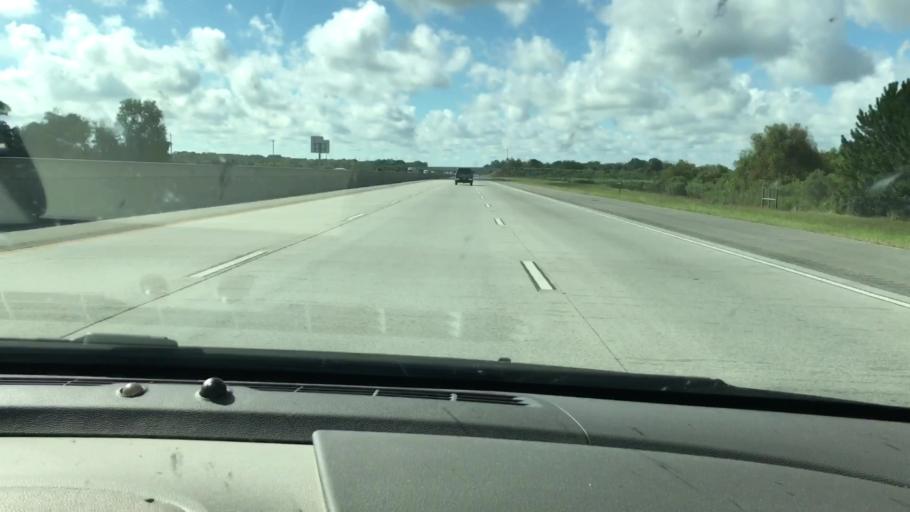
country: US
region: Georgia
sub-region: Tift County
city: Unionville
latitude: 31.3398
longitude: -83.4858
